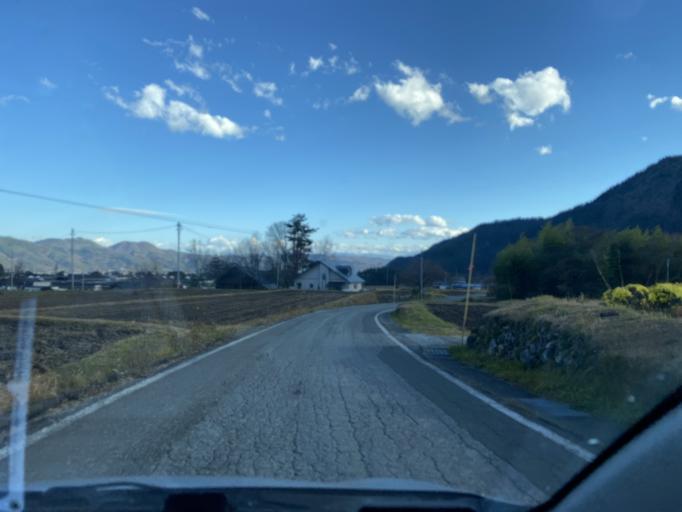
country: JP
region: Nagano
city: Omachi
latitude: 36.5213
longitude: 137.8015
